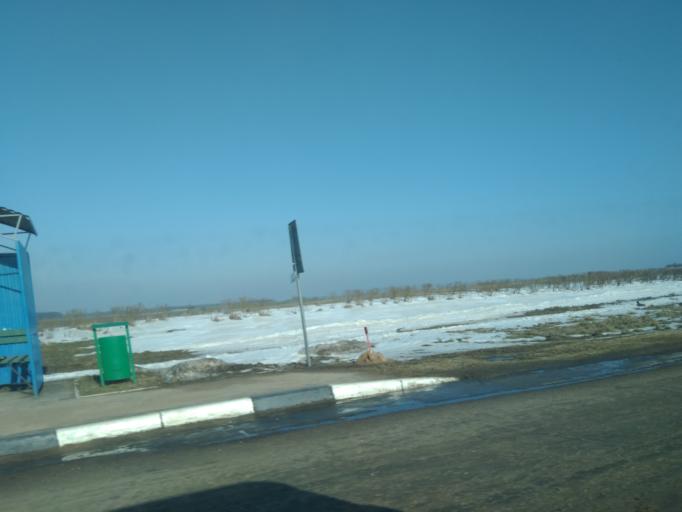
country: BY
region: Minsk
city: Snow
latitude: 53.2093
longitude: 26.4748
